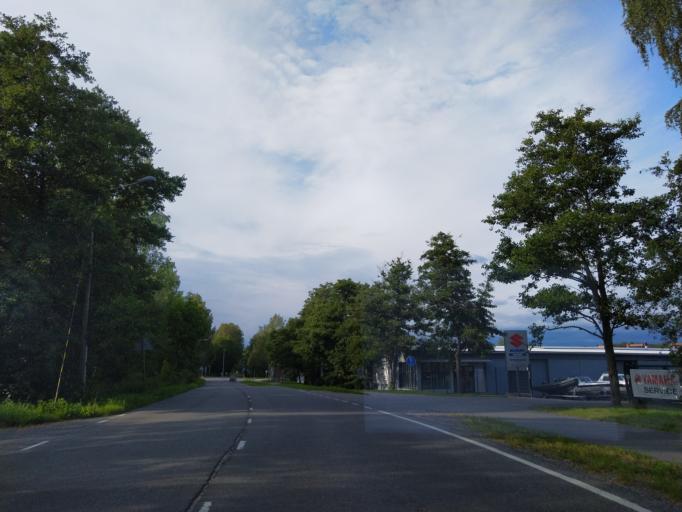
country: FI
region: Varsinais-Suomi
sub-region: Turku
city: Turku
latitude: 60.4254
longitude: 22.2270
